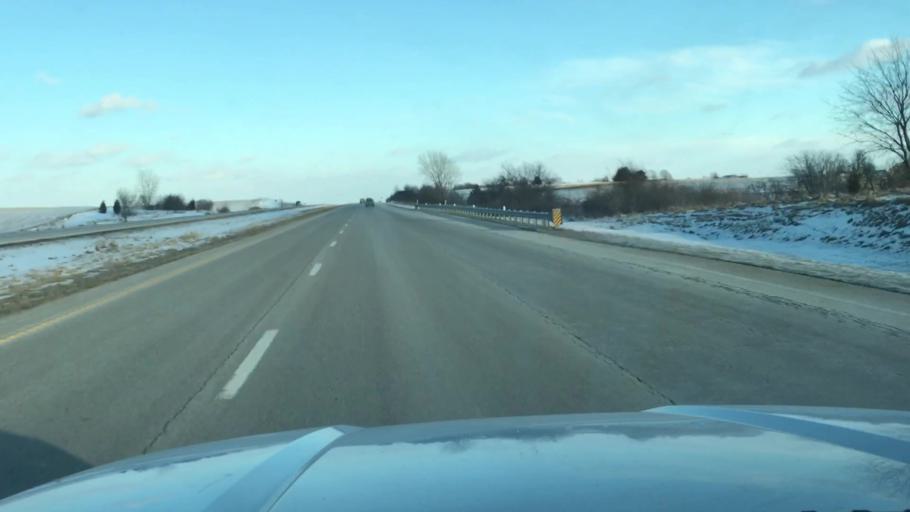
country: US
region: Missouri
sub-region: Andrew County
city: Country Club Village
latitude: 39.7475
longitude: -94.6920
